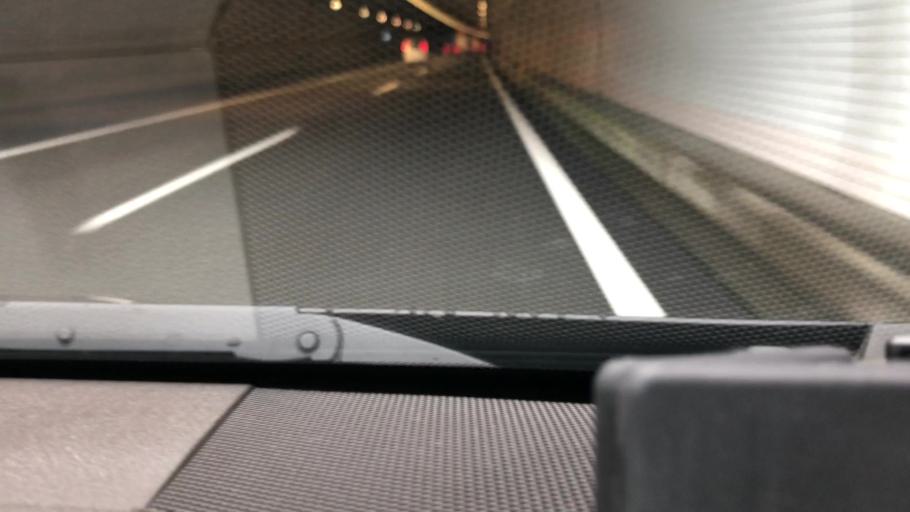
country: JP
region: Shizuoka
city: Fujieda
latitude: 34.9414
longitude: 138.2791
